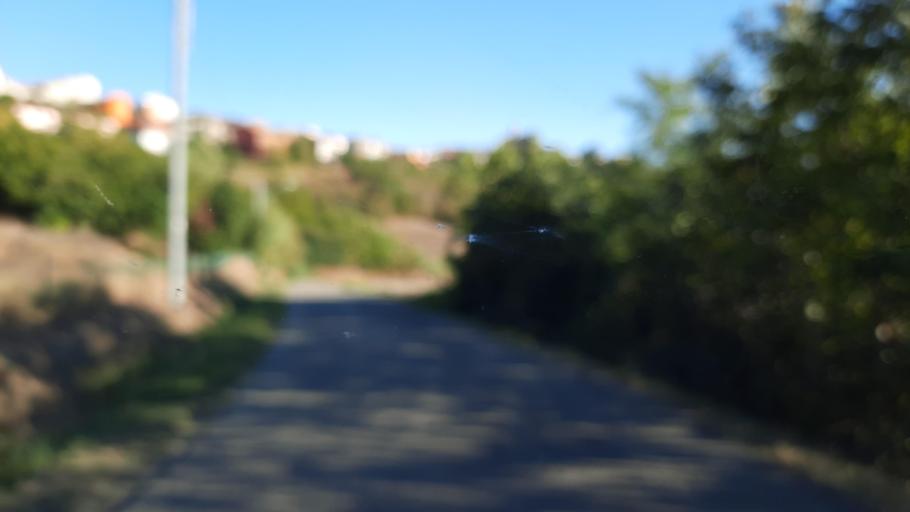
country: IT
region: Piedmont
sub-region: Provincia di Alessandria
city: Cuccaro Monferrato
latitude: 44.9959
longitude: 8.4527
